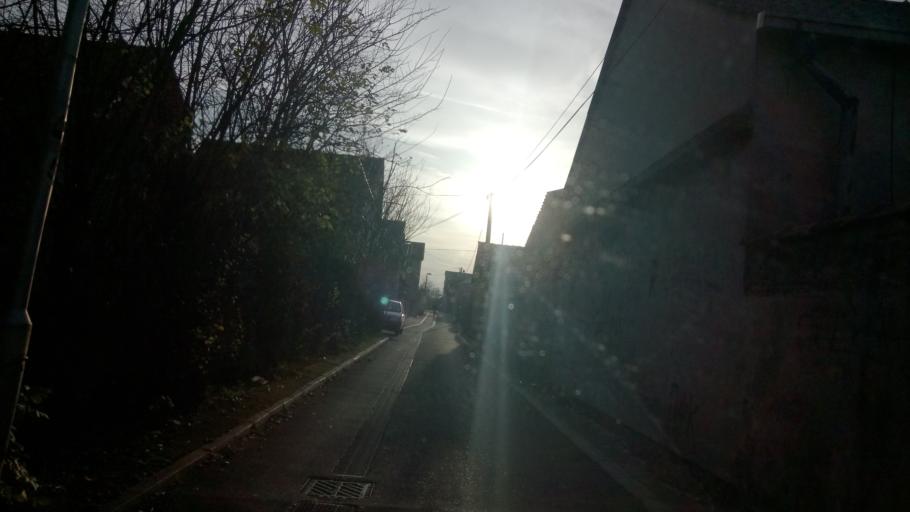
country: RS
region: Autonomna Pokrajina Vojvodina
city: Nova Pazova
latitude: 44.9429
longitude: 20.2251
